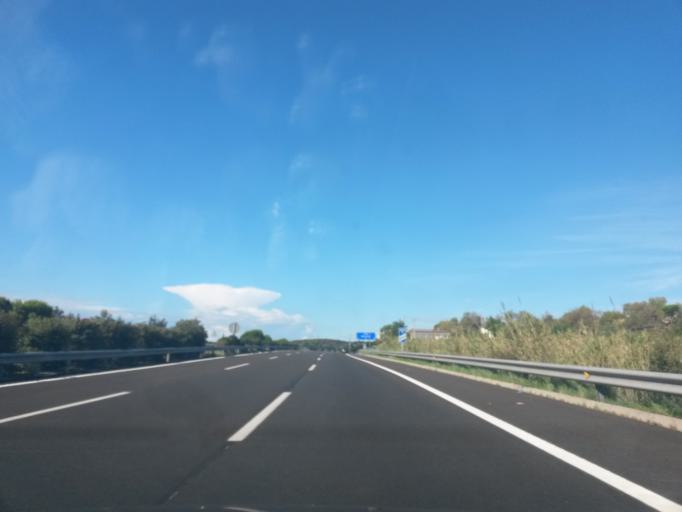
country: ES
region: Catalonia
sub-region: Provincia de Barcelona
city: Calella
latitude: 41.6282
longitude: 2.6599
